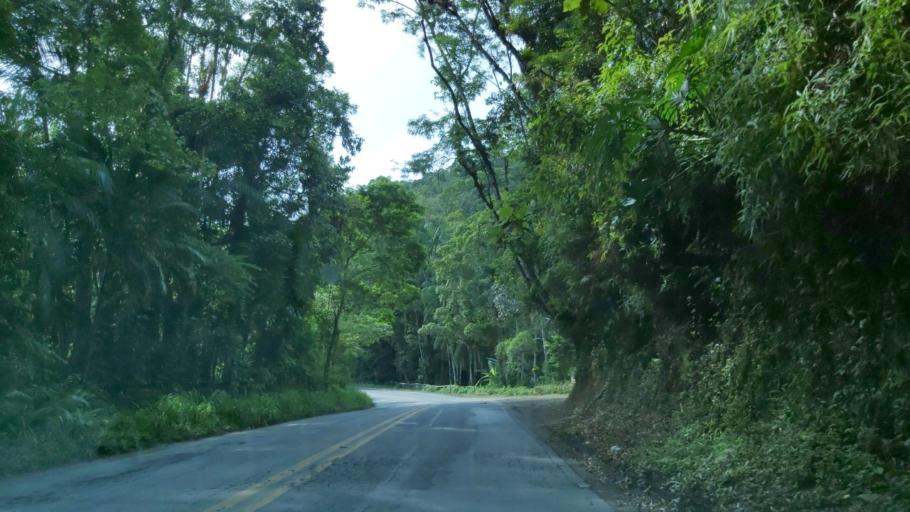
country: BR
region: Sao Paulo
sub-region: Miracatu
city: Miracatu
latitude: -24.0578
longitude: -47.5777
